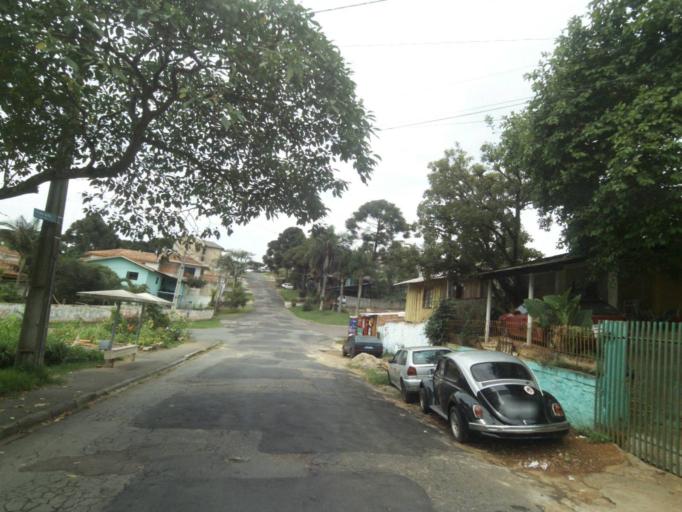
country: BR
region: Parana
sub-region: Curitiba
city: Curitiba
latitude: -25.3997
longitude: -49.3033
